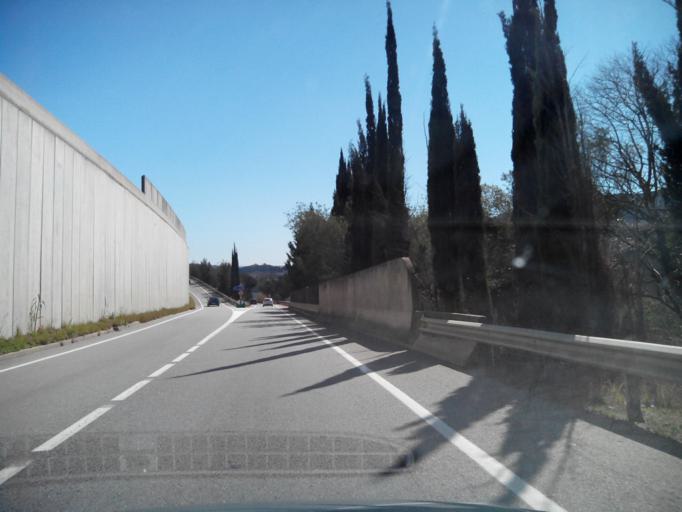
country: ES
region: Catalonia
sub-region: Provincia de Barcelona
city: Argentona
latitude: 41.5752
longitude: 2.3852
